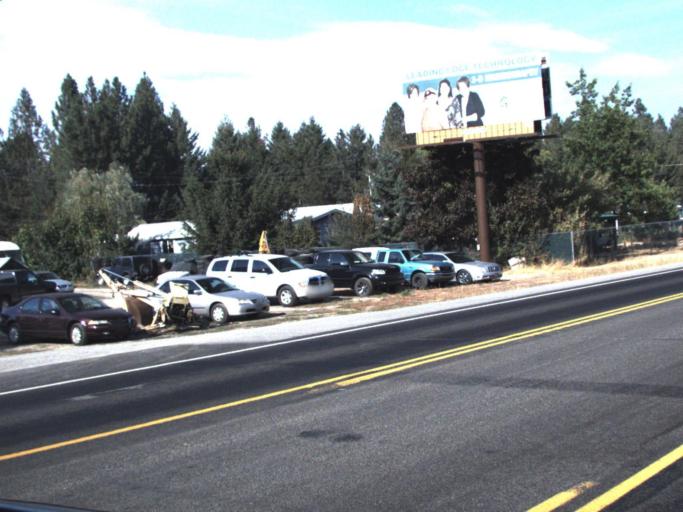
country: US
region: Washington
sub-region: Pend Oreille County
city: Newport
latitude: 48.1270
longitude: -117.1863
